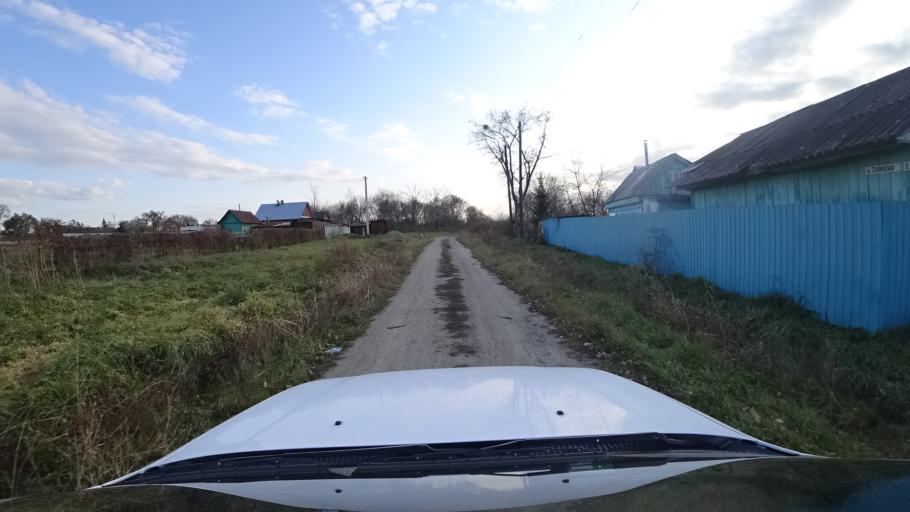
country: RU
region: Primorskiy
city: Lazo
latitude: 45.8240
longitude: 133.6101
